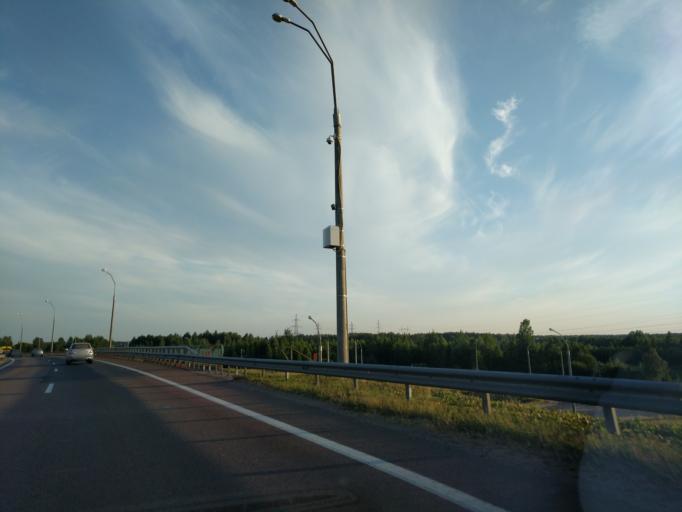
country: BY
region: Minsk
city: Bal'shavik
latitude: 53.9864
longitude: 27.5322
